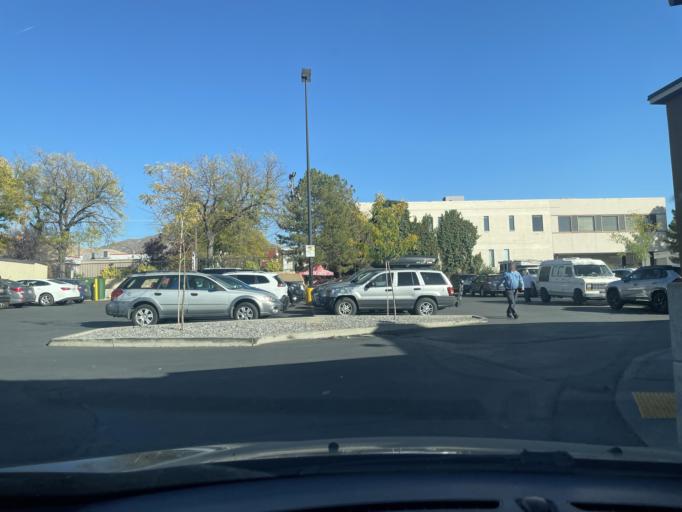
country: US
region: Utah
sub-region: Salt Lake County
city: Salt Lake City
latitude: 40.7600
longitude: -111.8726
